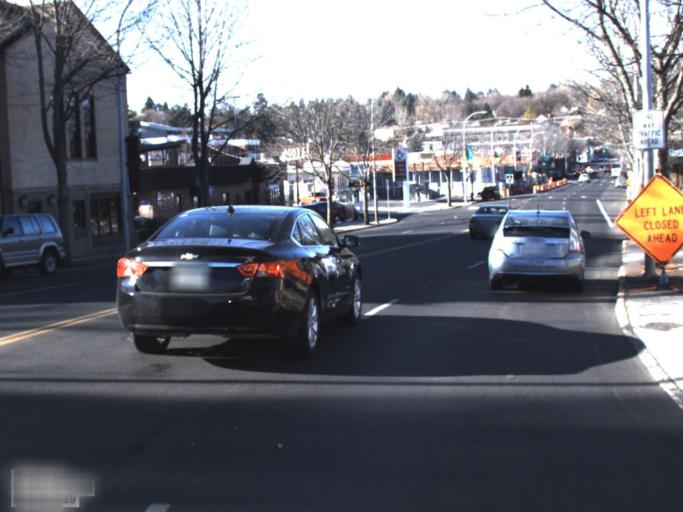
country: US
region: Washington
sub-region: Whitman County
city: Pullman
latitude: 46.7295
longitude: -117.1763
